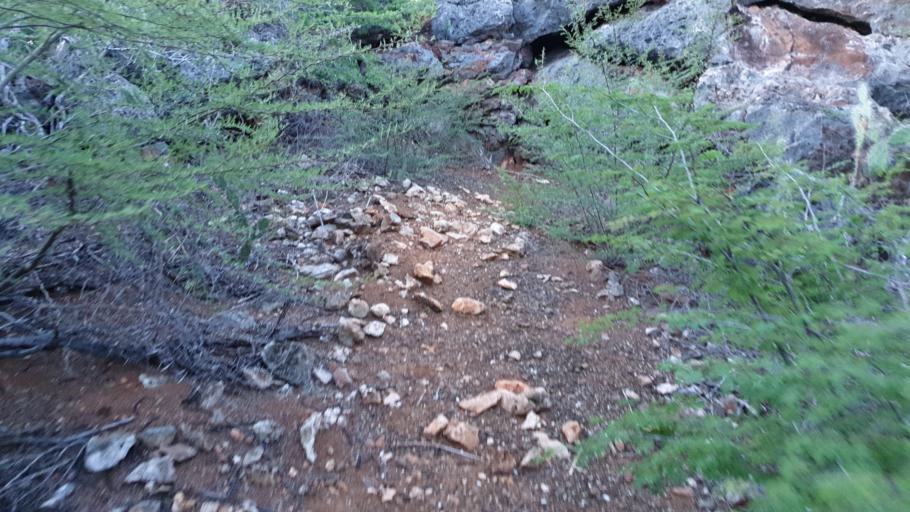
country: CW
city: Newport
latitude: 12.1304
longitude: -68.8145
